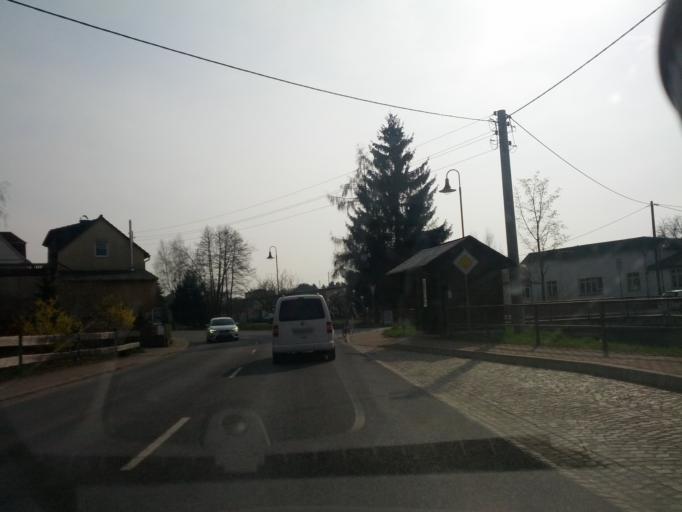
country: DE
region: Saxony
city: Kirchberg
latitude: 50.6010
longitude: 12.5472
